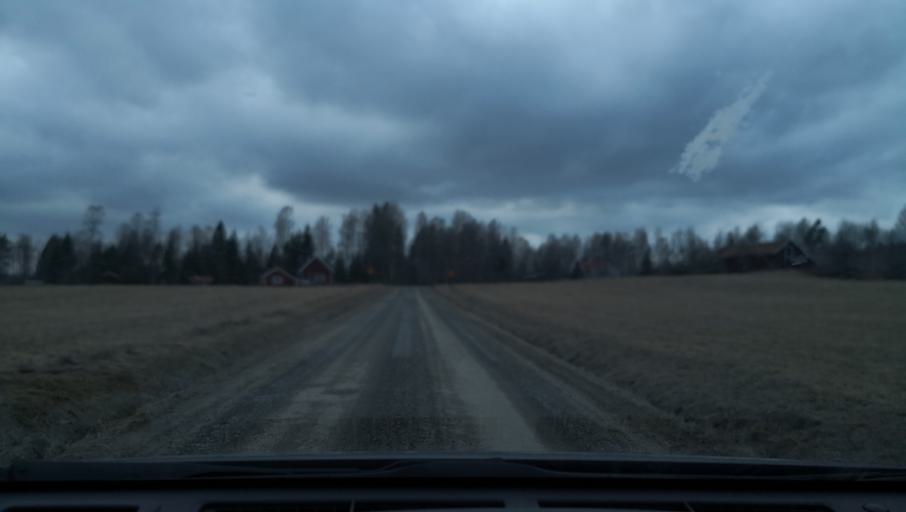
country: SE
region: Vaestmanland
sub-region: Kopings Kommun
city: Kolsva
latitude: 59.5999
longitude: 15.7087
